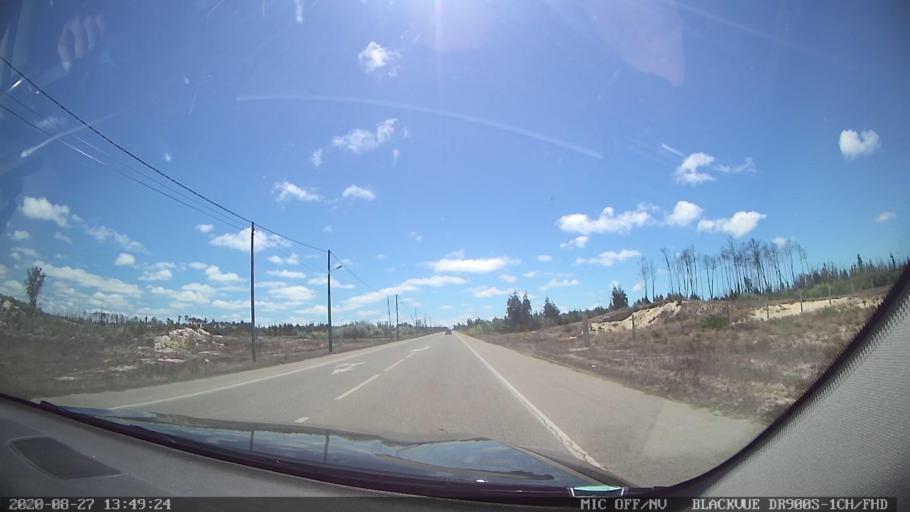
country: PT
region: Coimbra
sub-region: Mira
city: Mira
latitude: 40.3681
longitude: -8.7462
